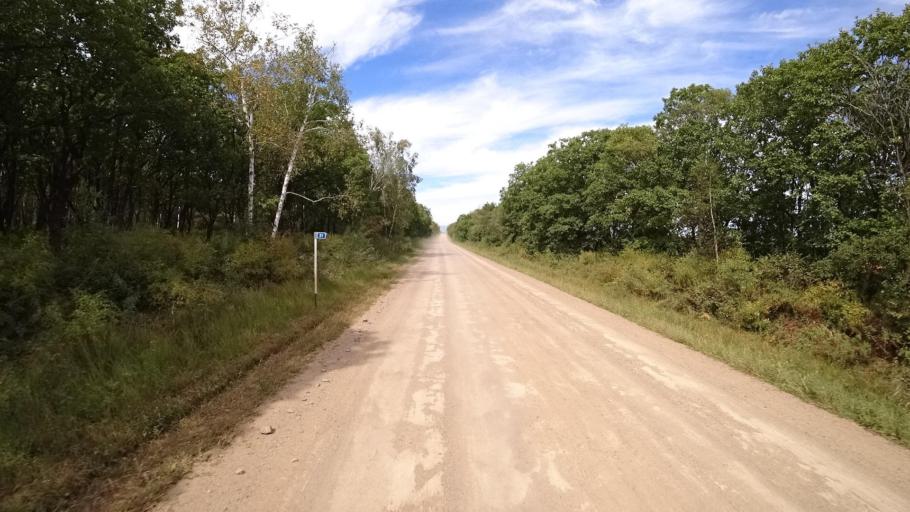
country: RU
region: Primorskiy
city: Yakovlevka
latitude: 44.5996
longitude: 133.6051
